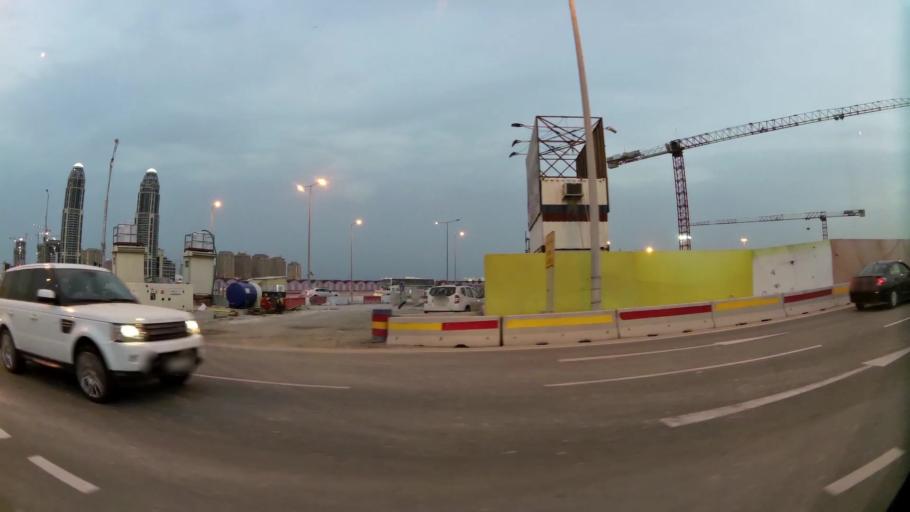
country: QA
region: Baladiyat ad Dawhah
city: Doha
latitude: 25.3722
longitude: 51.5248
